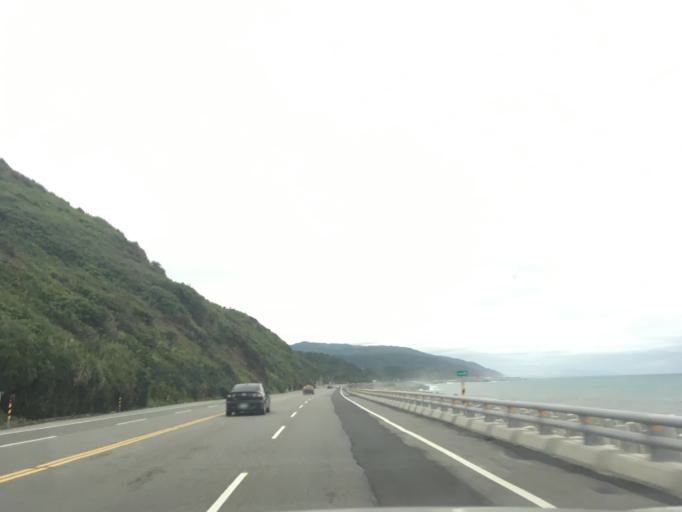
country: TW
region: Taiwan
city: Hengchun
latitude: 22.3182
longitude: 120.8916
